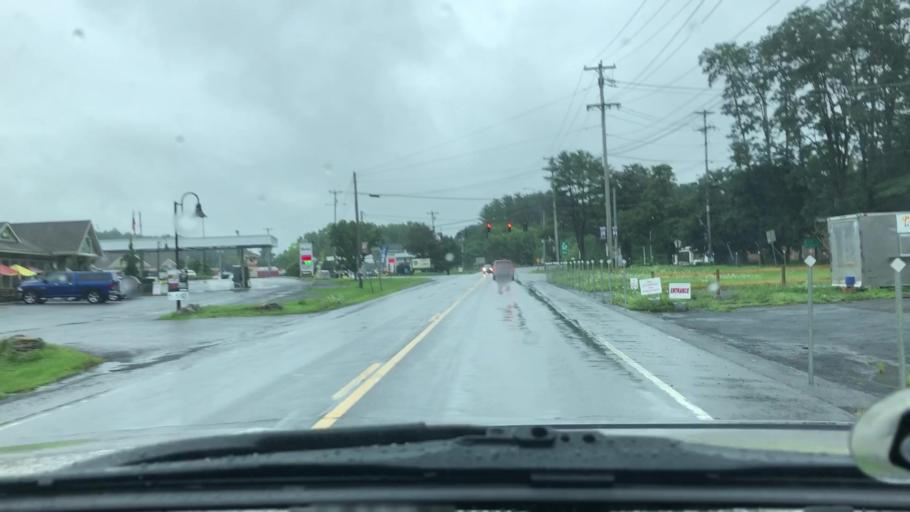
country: US
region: New York
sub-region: Greene County
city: Cairo
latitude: 42.2927
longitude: -73.9883
